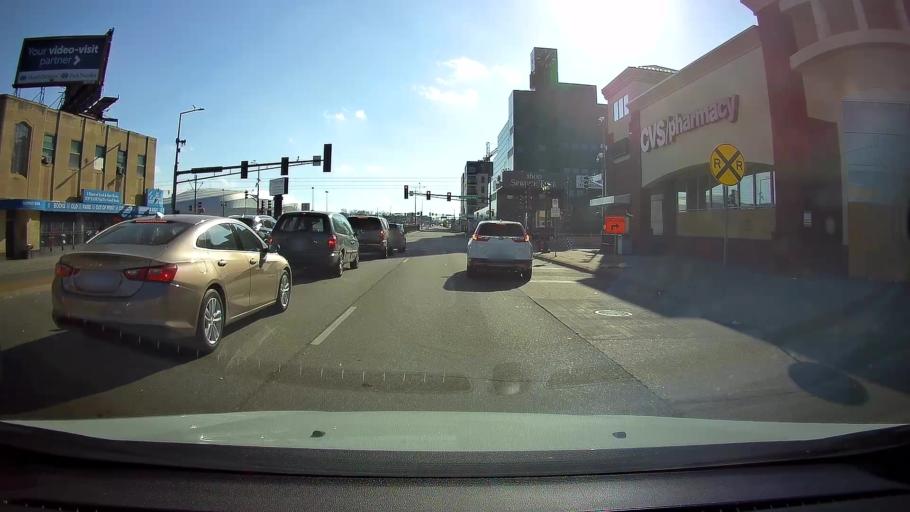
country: US
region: Minnesota
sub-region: Ramsey County
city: Falcon Heights
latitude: 44.9562
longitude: -93.1671
